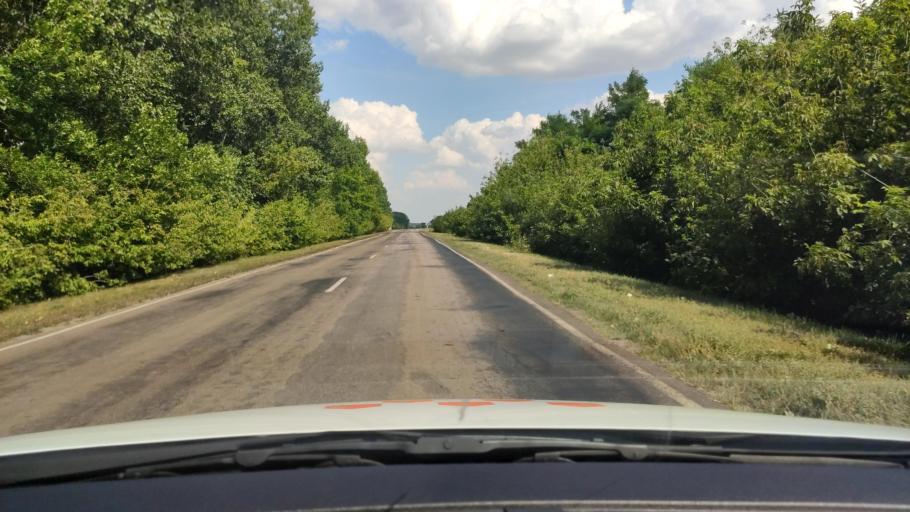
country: RU
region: Voronezj
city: Ertil'
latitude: 51.7896
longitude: 40.6561
